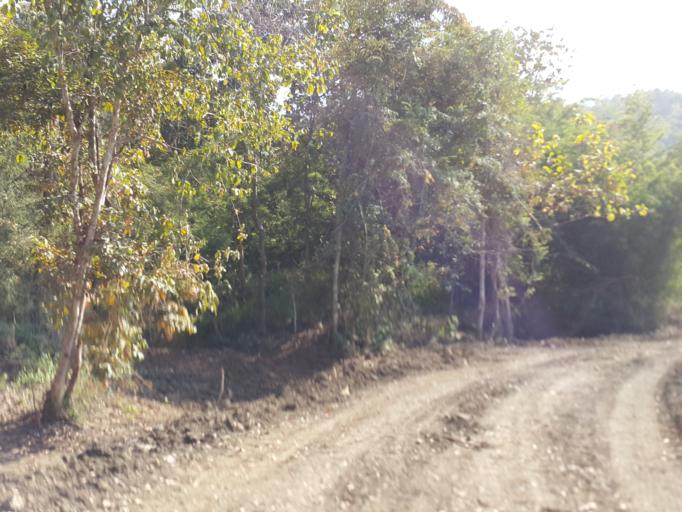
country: TH
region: Chiang Mai
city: Mae On
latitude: 18.8362
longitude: 99.2375
